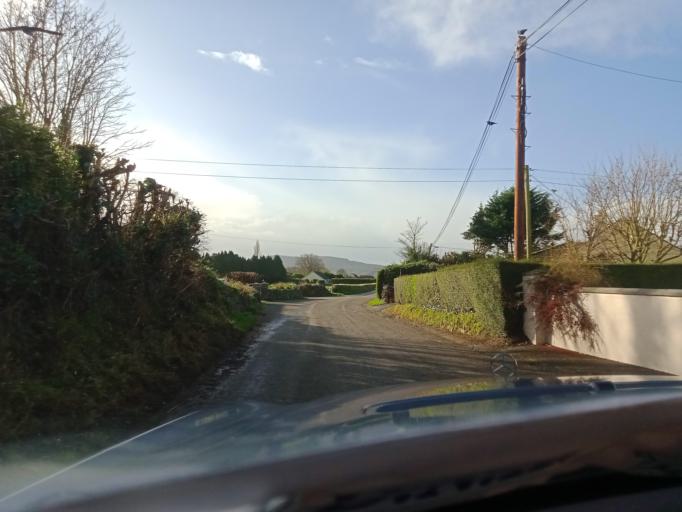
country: IE
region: Leinster
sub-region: Kilkenny
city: Mooncoin
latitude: 52.2927
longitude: -7.2660
